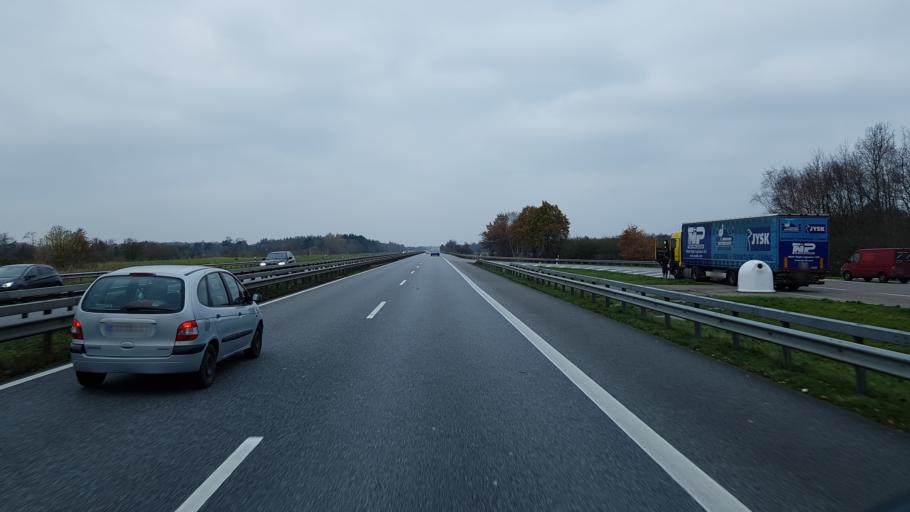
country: DE
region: Lower Saxony
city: Uthlede
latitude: 53.3413
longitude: 8.6070
